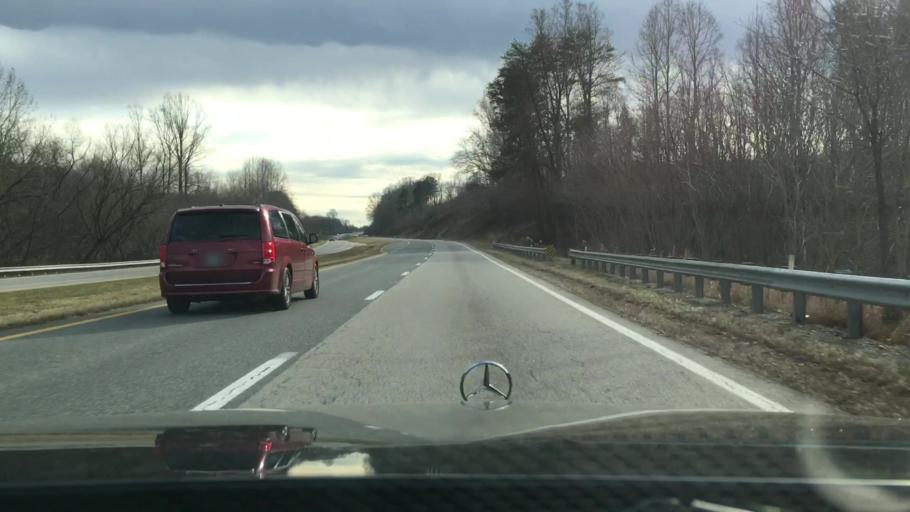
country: US
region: Virginia
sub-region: Pittsylvania County
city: Motley
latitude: 37.0175
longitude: -79.3576
